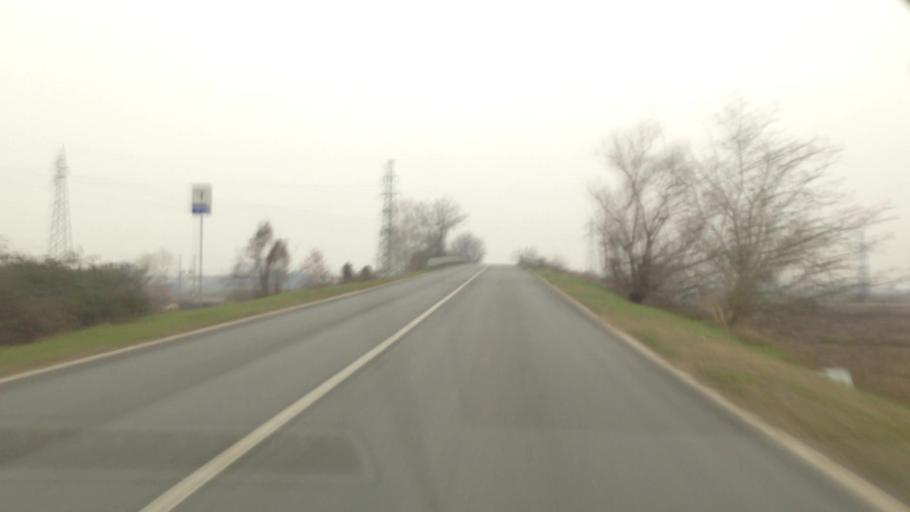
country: IT
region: Piedmont
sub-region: Provincia di Vercelli
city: Livorno Ferraris
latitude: 45.2801
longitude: 8.0670
